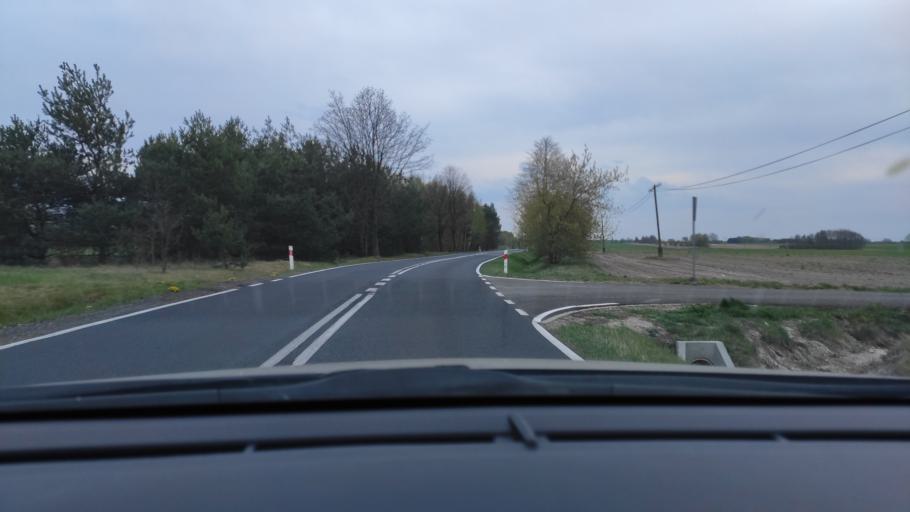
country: PL
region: Masovian Voivodeship
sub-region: Powiat zwolenski
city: Zwolen
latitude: 51.3796
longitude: 21.5624
